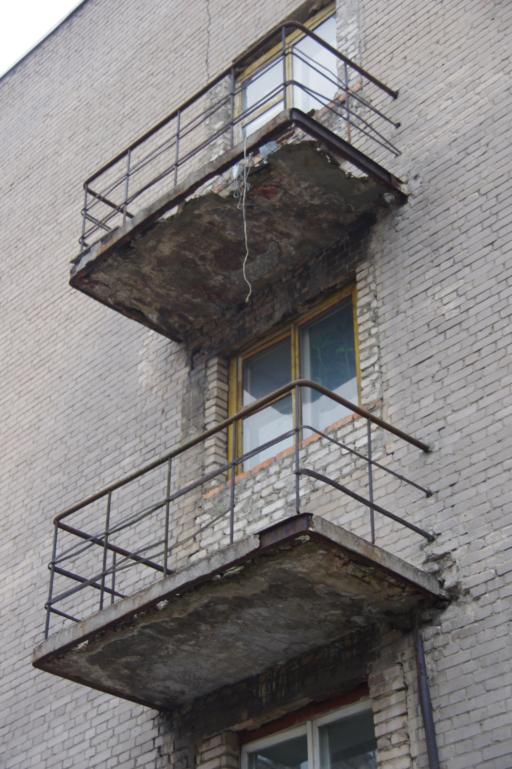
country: RU
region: Moskovskaya
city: Yubileyny
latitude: 55.9168
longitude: 37.8550
